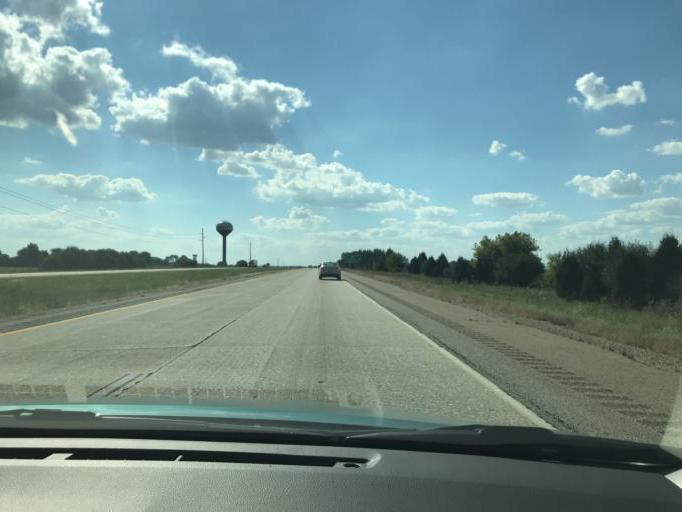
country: US
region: Wisconsin
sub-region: Walworth County
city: Darien
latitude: 42.6129
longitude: -88.7117
